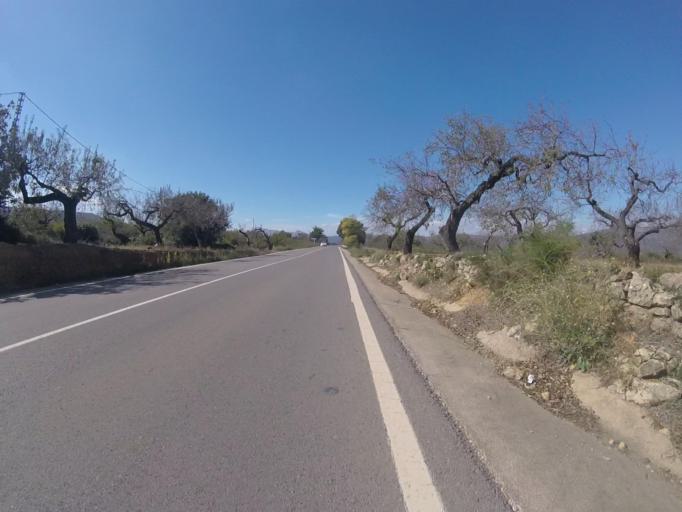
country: ES
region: Valencia
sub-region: Provincia de Castello
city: Albocasser
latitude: 40.3536
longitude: 0.0190
